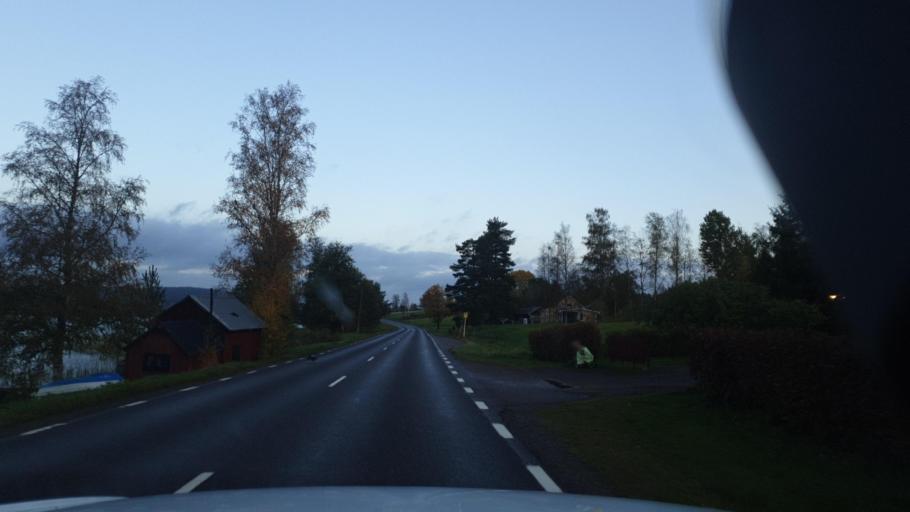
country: SE
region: Vaermland
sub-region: Arvika Kommun
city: Arvika
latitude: 59.7411
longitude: 12.5575
